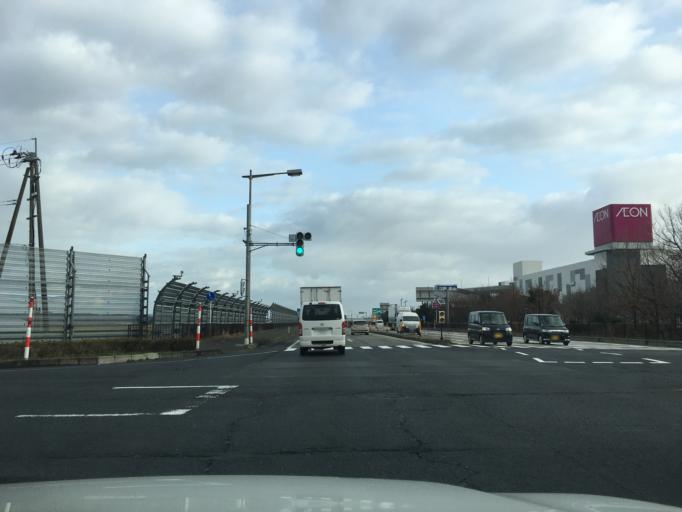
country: JP
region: Yamagata
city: Tsuruoka
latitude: 38.8143
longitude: 139.8327
